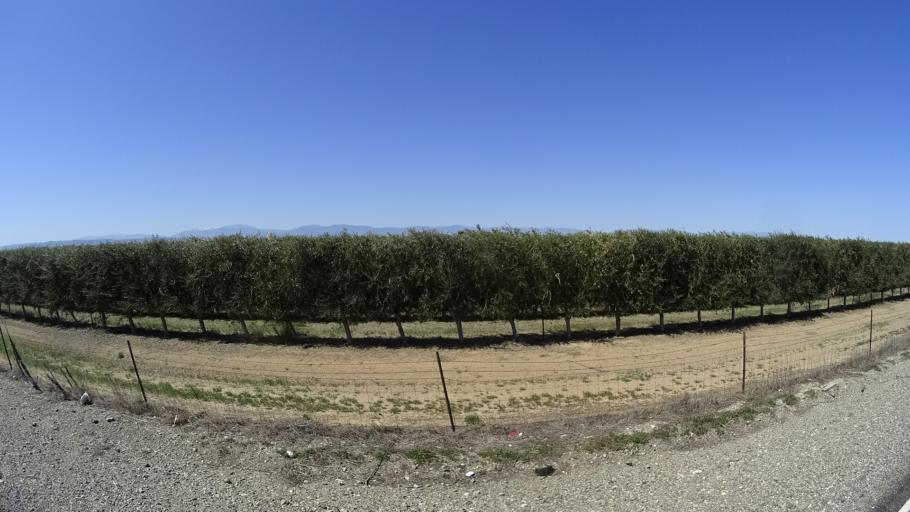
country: US
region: California
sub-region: Glenn County
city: Willows
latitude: 39.5964
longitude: -122.2498
